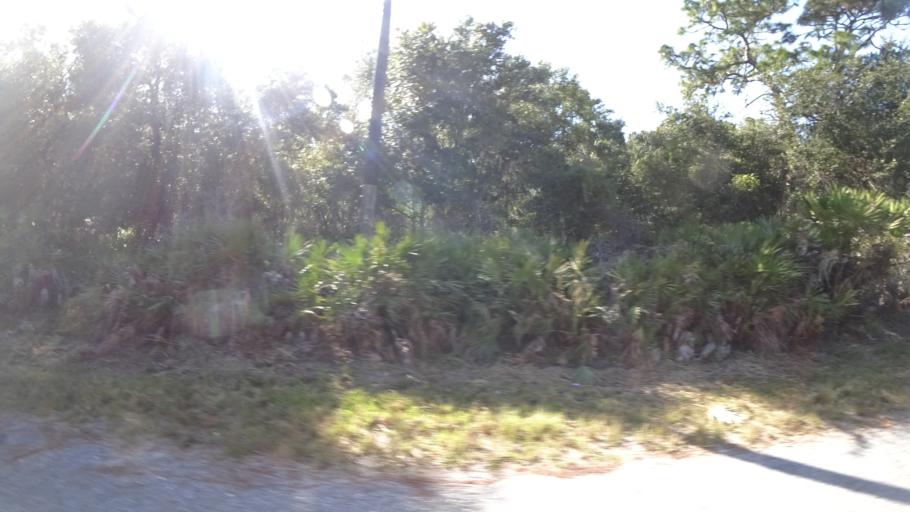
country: US
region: Florida
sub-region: Sarasota County
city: The Meadows
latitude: 27.4139
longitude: -82.4504
